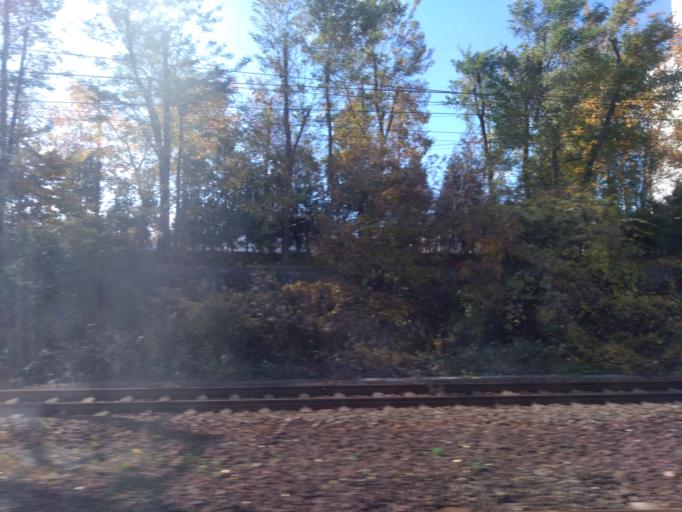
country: JP
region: Hokkaido
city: Kitahiroshima
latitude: 42.9765
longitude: 141.5635
